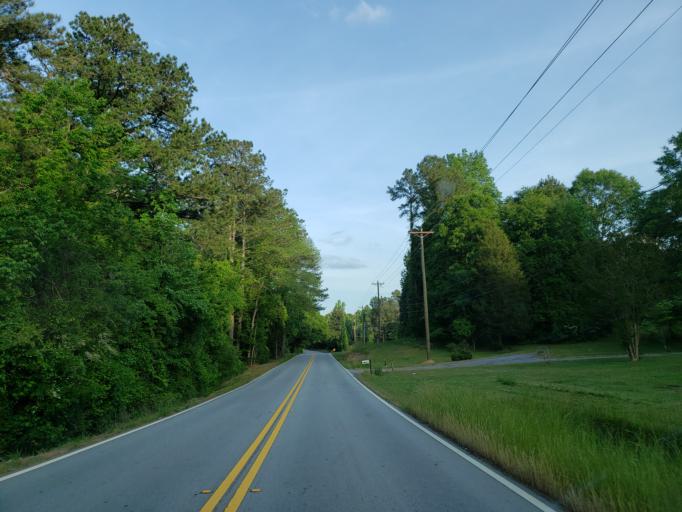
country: US
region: Georgia
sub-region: Carroll County
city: Carrollton
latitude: 33.5950
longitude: -85.1330
